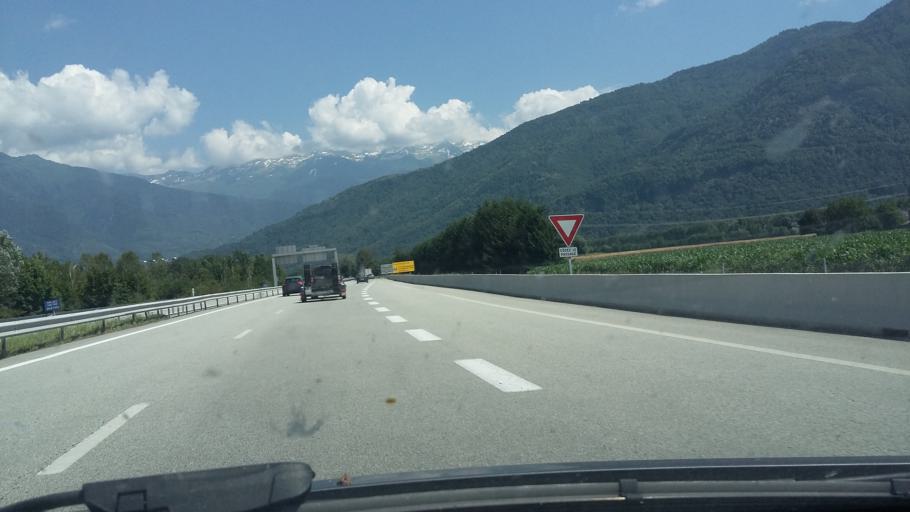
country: FR
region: Rhone-Alpes
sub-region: Departement de la Savoie
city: Aiton
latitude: 45.5655
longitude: 6.2236
